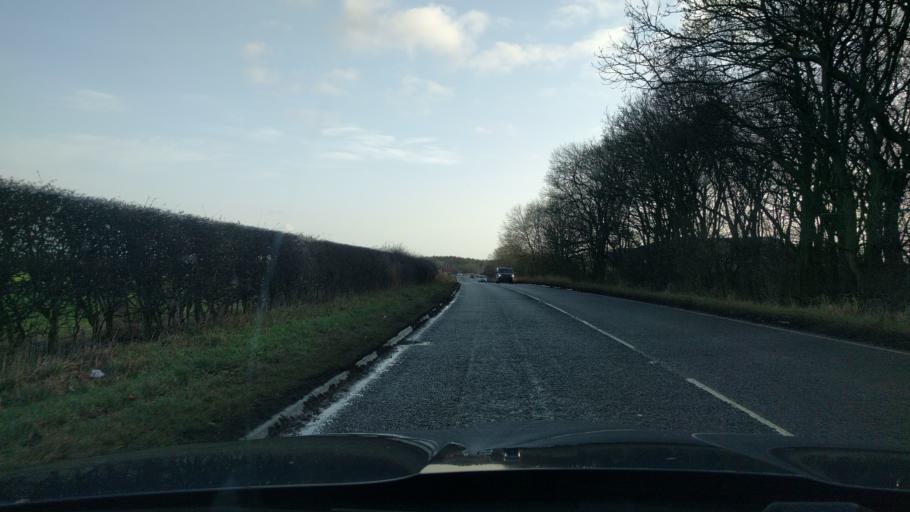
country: GB
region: England
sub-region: Northumberland
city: Cresswell
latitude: 55.1984
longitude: -1.5555
